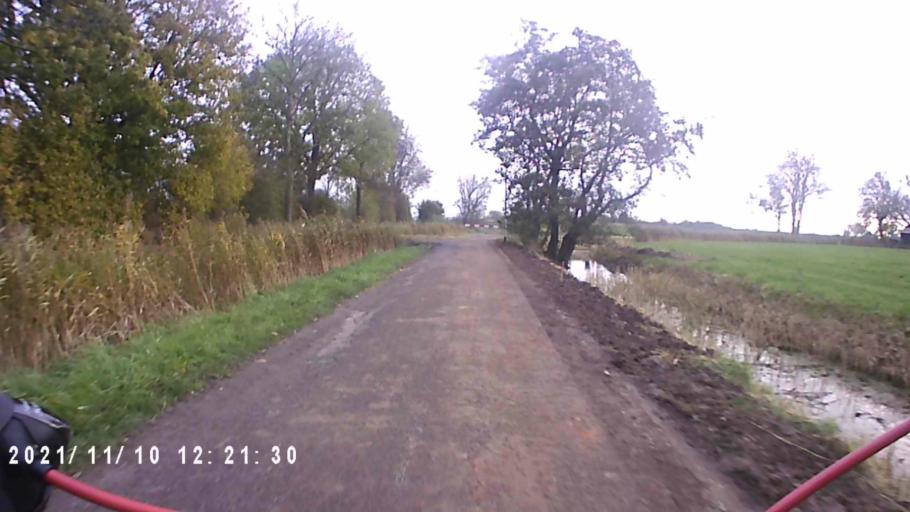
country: NL
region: Groningen
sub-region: Gemeente Winsum
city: Winsum
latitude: 53.2953
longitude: 6.5387
